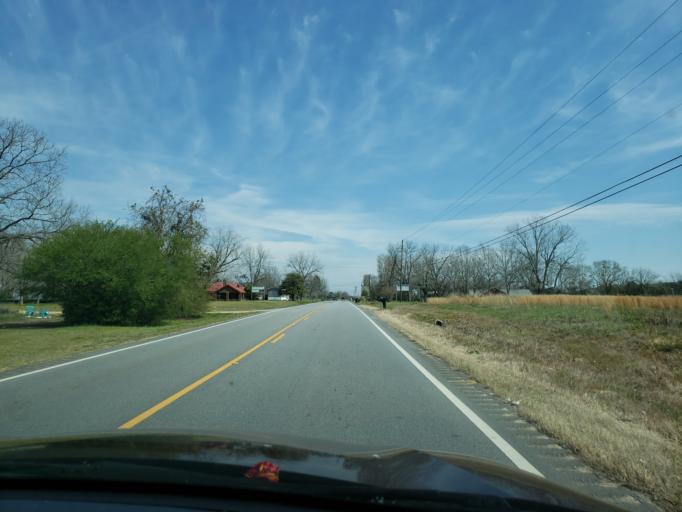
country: US
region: Alabama
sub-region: Elmore County
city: Tallassee
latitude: 32.5600
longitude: -85.8110
